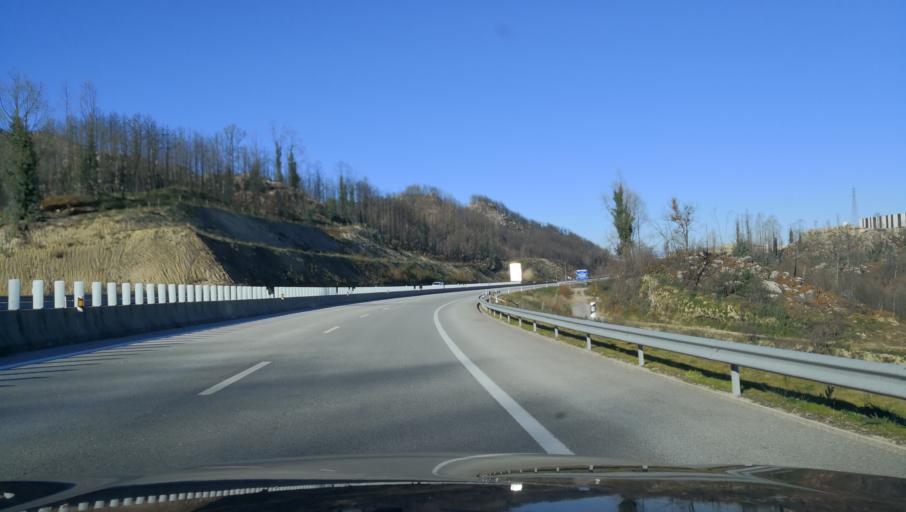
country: PT
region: Viseu
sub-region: Vouzela
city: Vouzela
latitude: 40.6548
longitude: -8.0760
